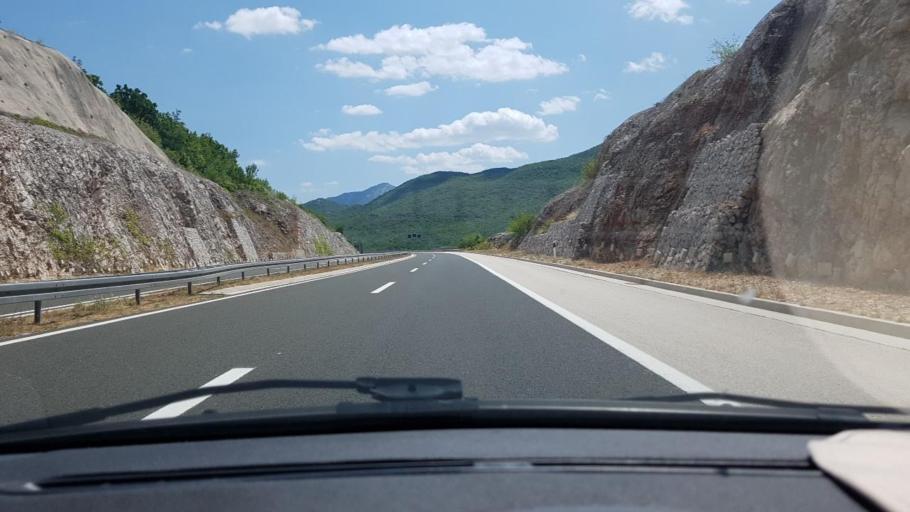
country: HR
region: Splitsko-Dalmatinska
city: Grubine
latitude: 43.3703
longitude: 17.0908
